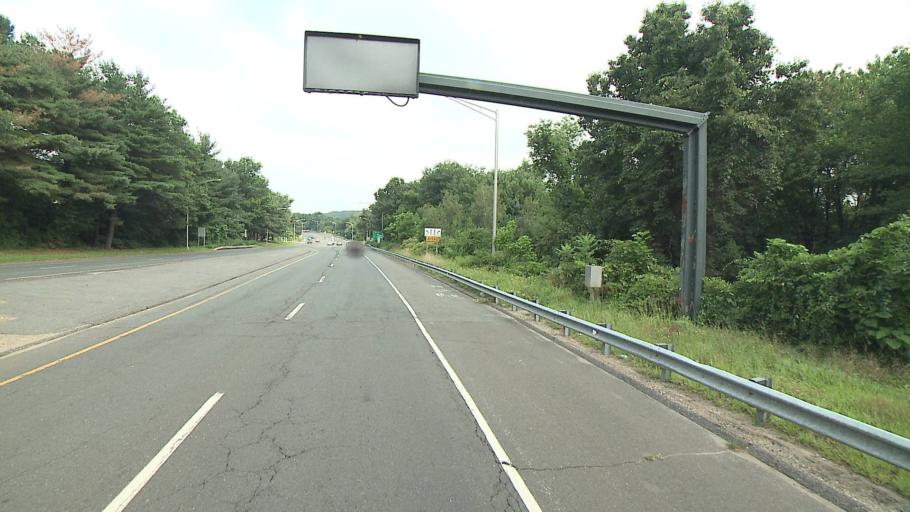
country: US
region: Connecticut
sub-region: New Haven County
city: Waterbury
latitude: 41.5693
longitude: -73.0588
